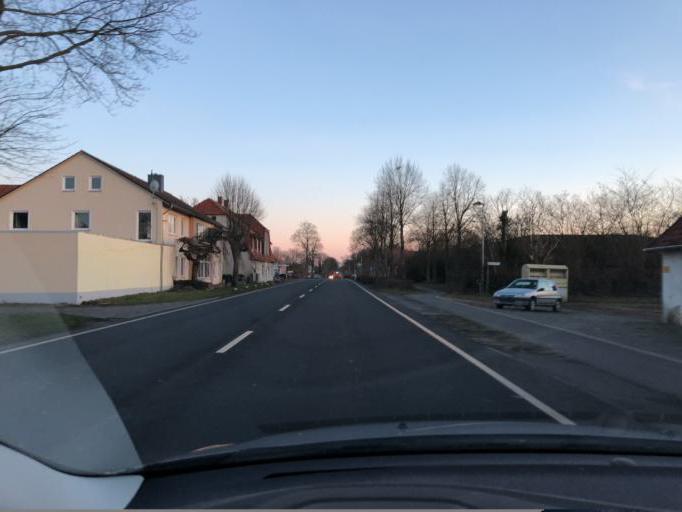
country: DE
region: Lower Saxony
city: Wietzen
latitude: 52.7076
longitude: 9.0760
